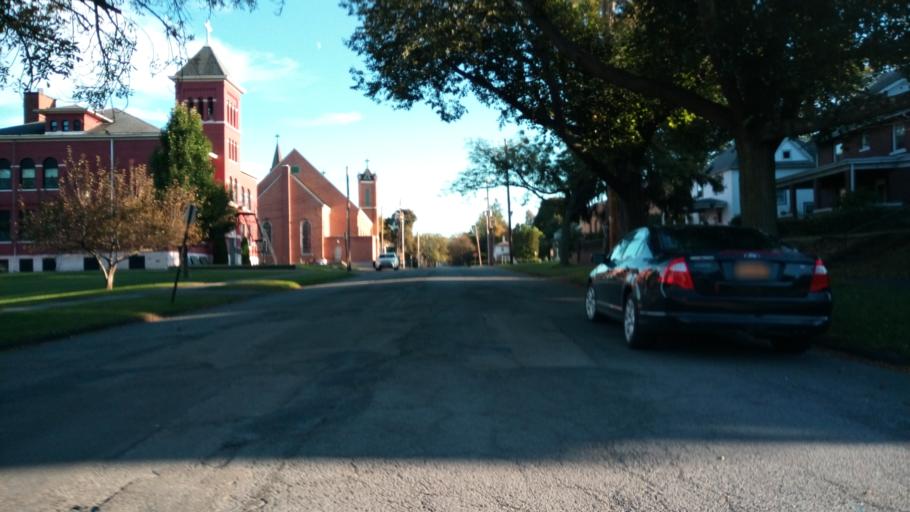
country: US
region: New York
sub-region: Chemung County
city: Elmira
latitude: 42.0780
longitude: -76.8069
